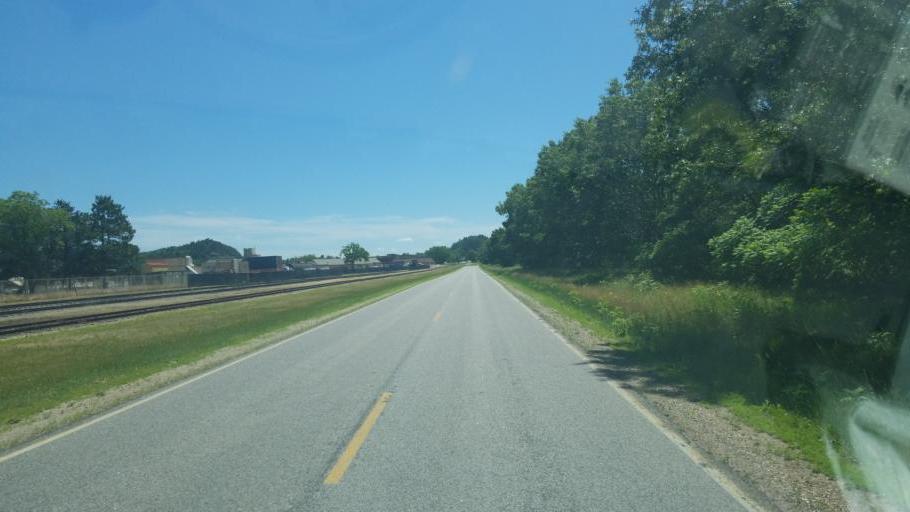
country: US
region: Wisconsin
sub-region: Juneau County
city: New Lisbon
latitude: 43.9321
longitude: -90.2775
